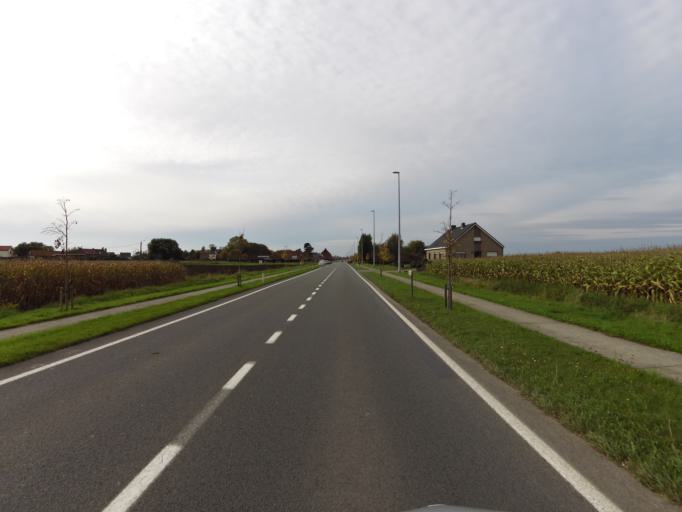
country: BE
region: Flanders
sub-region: Provincie West-Vlaanderen
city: Ichtegem
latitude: 51.1219
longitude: 3.0683
